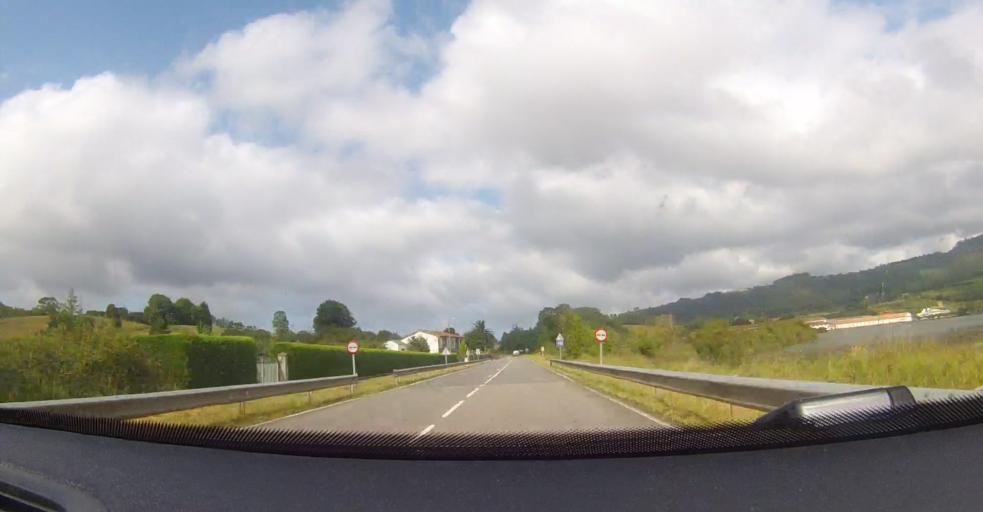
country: ES
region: Asturias
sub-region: Province of Asturias
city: Villaviciosa
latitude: 43.4937
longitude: -5.4315
